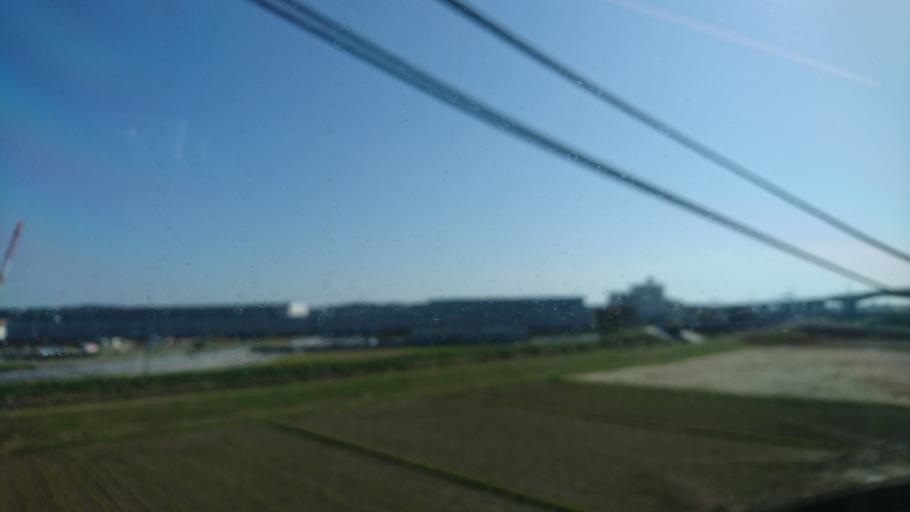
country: JP
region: Miyagi
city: Rifu
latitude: 38.3214
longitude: 140.9685
